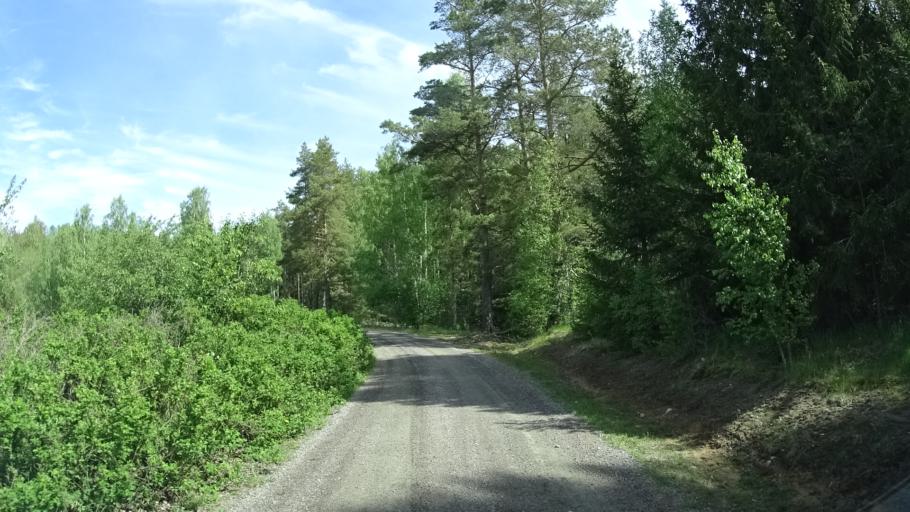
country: SE
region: OEstergoetland
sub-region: Finspangs Kommun
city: Finspang
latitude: 58.7881
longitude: 15.8717
